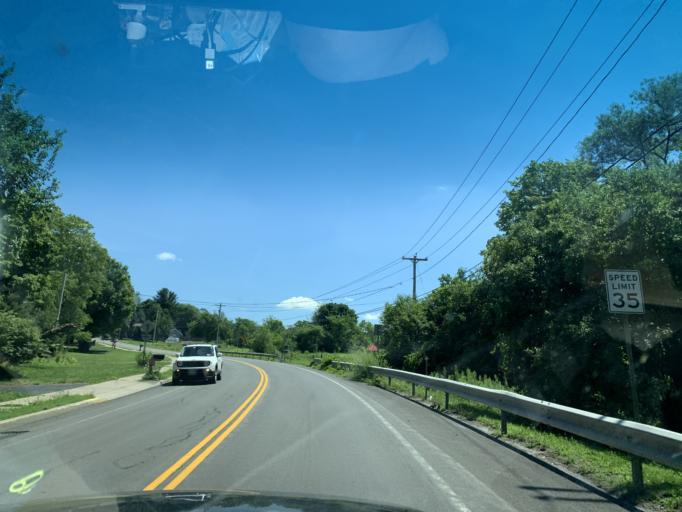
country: US
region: New York
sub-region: Oneida County
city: Washington Mills
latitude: 43.0516
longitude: -75.2688
